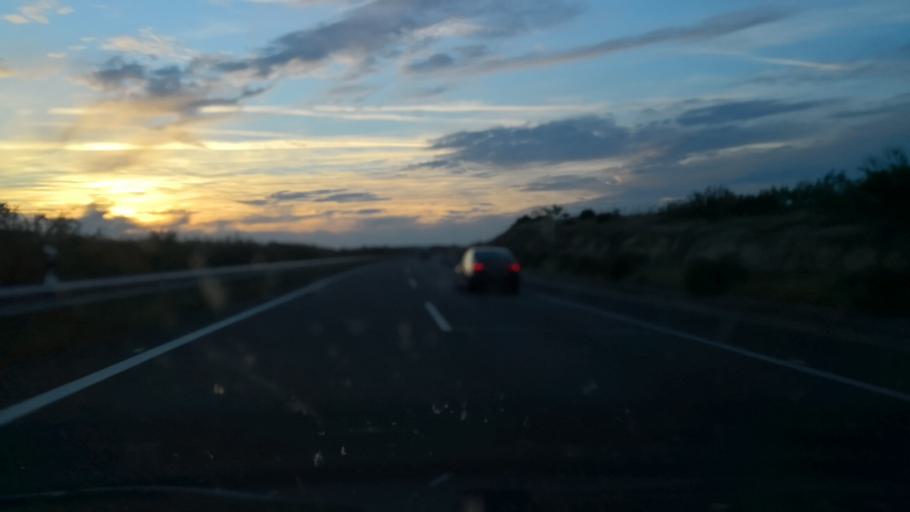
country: ES
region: Extremadura
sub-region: Provincia de Caceres
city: Caceres
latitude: 39.3931
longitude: -6.3734
